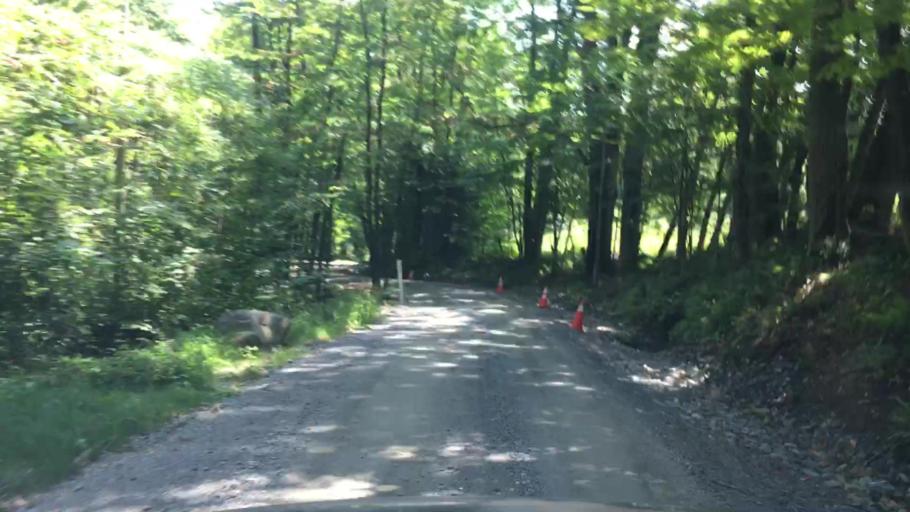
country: US
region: Vermont
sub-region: Windham County
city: West Brattleboro
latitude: 42.7992
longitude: -72.6417
